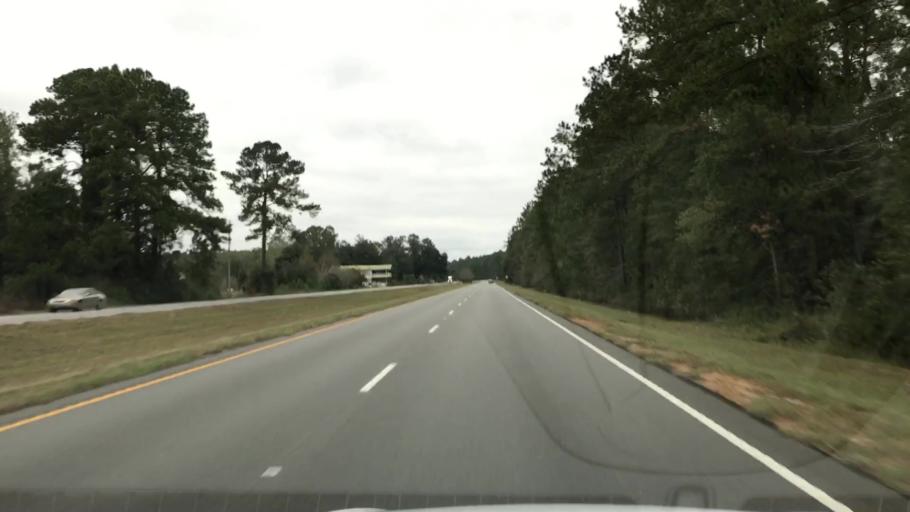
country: US
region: South Carolina
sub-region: Georgetown County
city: Georgetown
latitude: 33.2255
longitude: -79.3777
